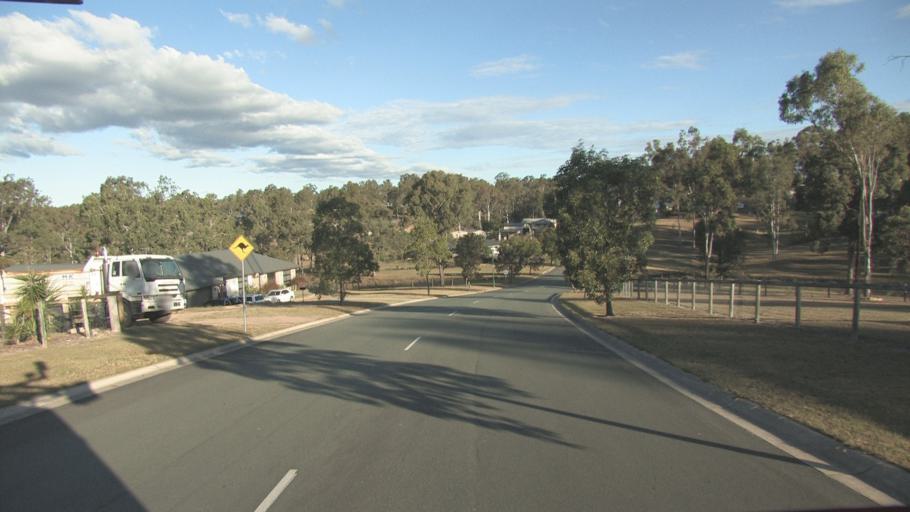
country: AU
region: Queensland
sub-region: Logan
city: Cedar Vale
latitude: -27.8710
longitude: 153.0763
